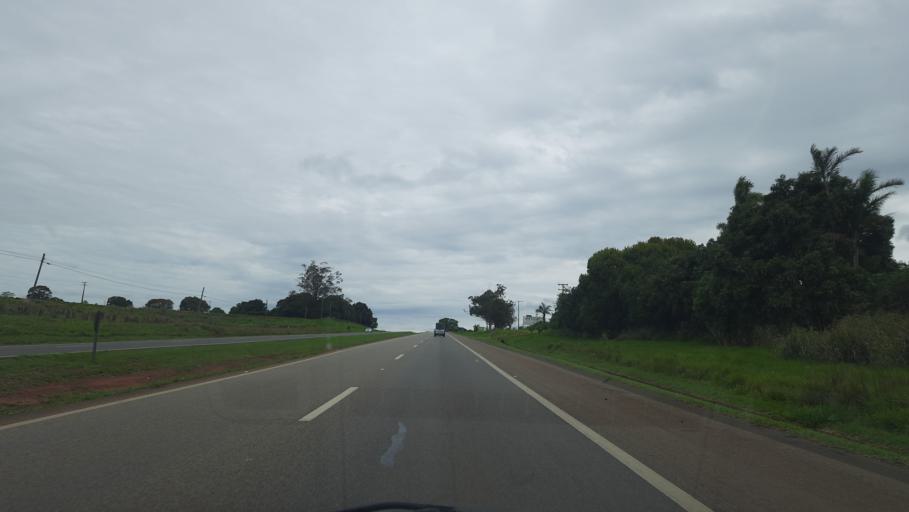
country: BR
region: Sao Paulo
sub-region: Moji-Guacu
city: Mogi-Gaucu
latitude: -22.2498
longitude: -46.9778
